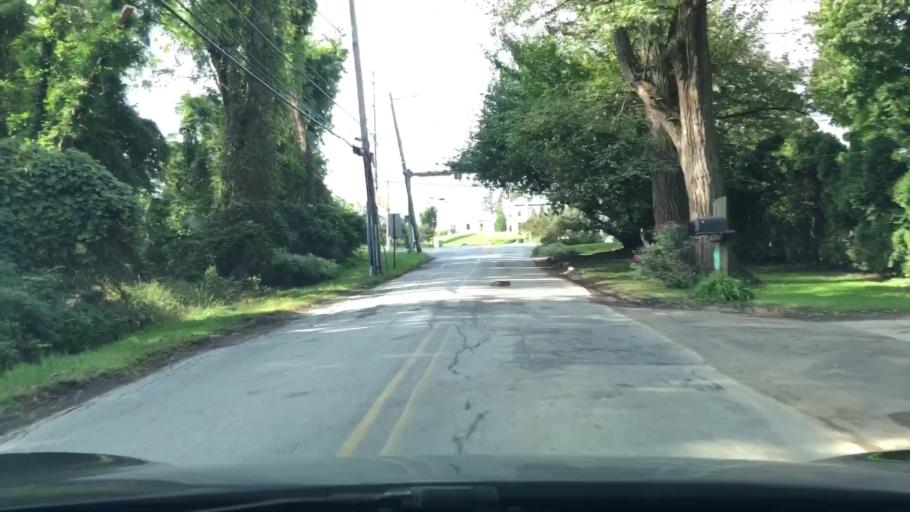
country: US
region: Pennsylvania
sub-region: Delaware County
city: Wayne
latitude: 40.0008
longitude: -75.4095
